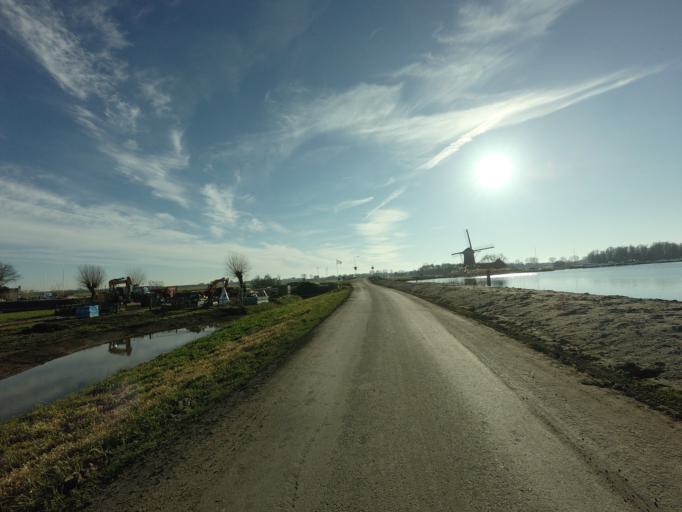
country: NL
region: South Holland
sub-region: Gemeente Leiderdorp
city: Leiderdorp
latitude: 52.1874
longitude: 4.5259
